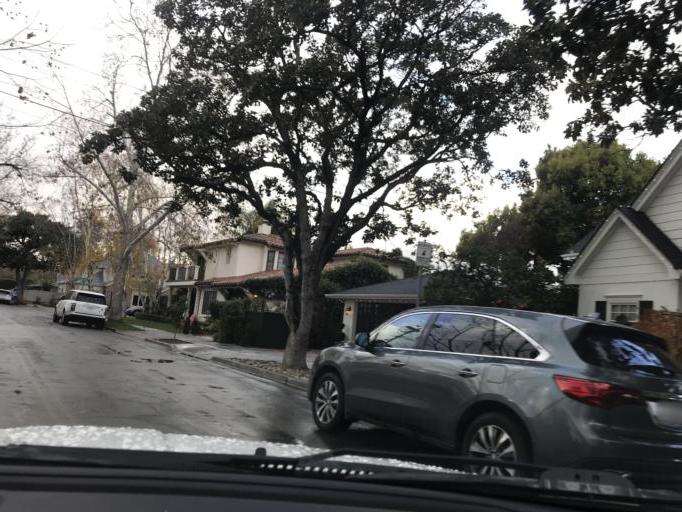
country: US
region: California
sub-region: Santa Clara County
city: Buena Vista
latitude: 37.3057
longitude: -121.9022
